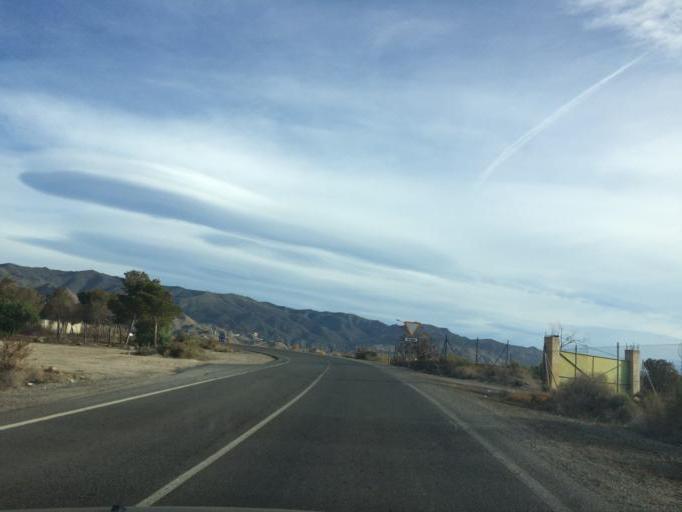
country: ES
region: Andalusia
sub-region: Provincia de Almeria
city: Pechina
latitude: 36.9250
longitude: -2.4393
